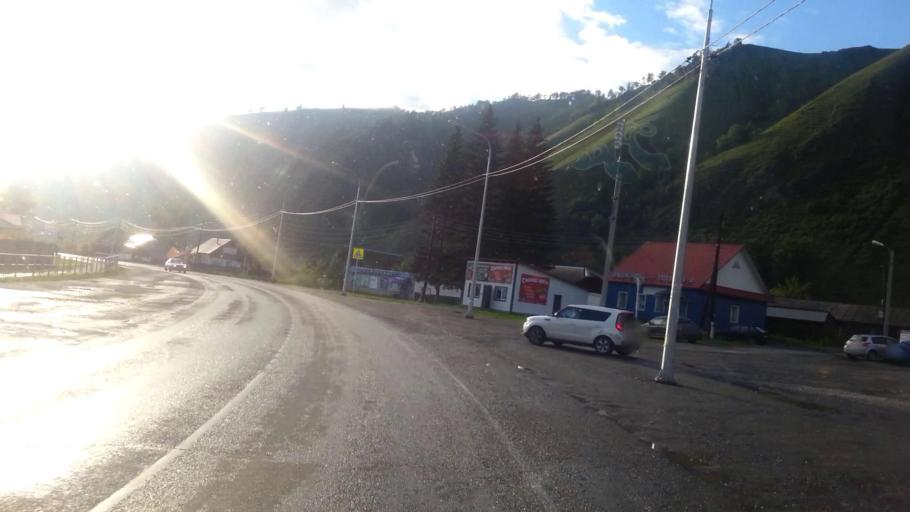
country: RU
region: Altay
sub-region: Mayminskiy Rayon
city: Manzherok
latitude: 51.8336
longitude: 85.7807
